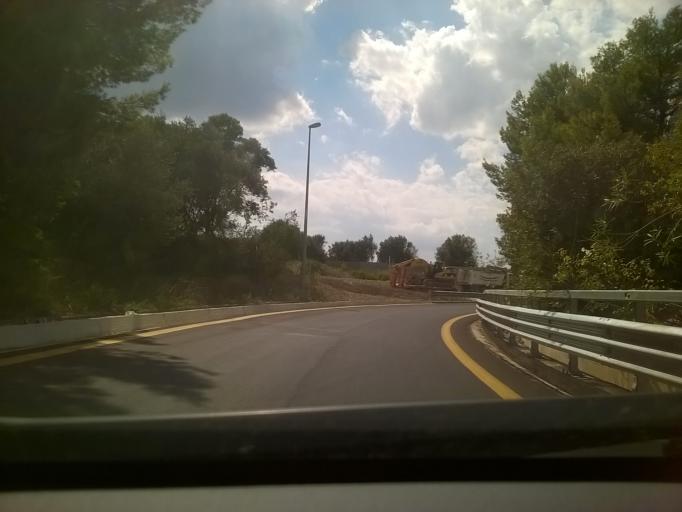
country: IT
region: Apulia
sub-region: Provincia di Taranto
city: Taranto
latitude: 40.4631
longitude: 17.2888
